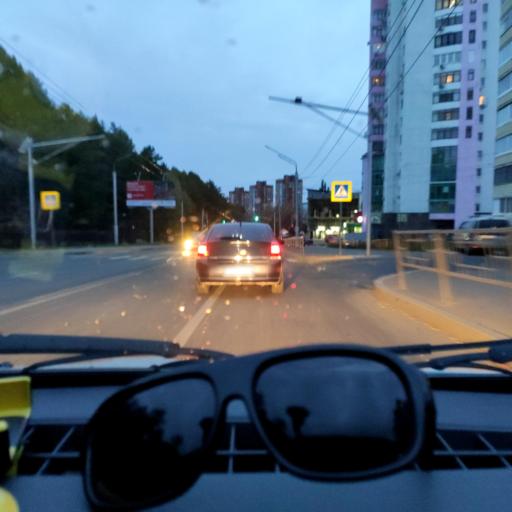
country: RU
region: Bashkortostan
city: Ufa
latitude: 54.6947
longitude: 56.0041
